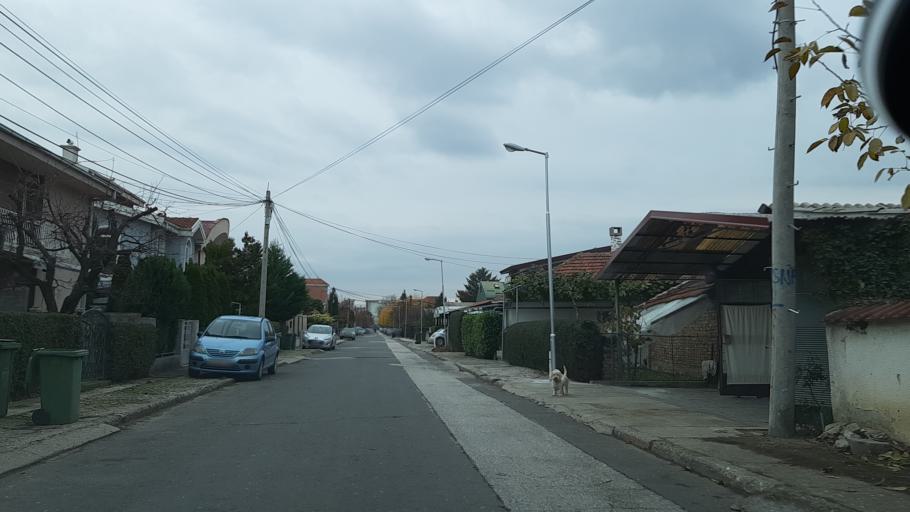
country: MK
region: Kisela Voda
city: Usje
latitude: 41.9729
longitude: 21.4702
